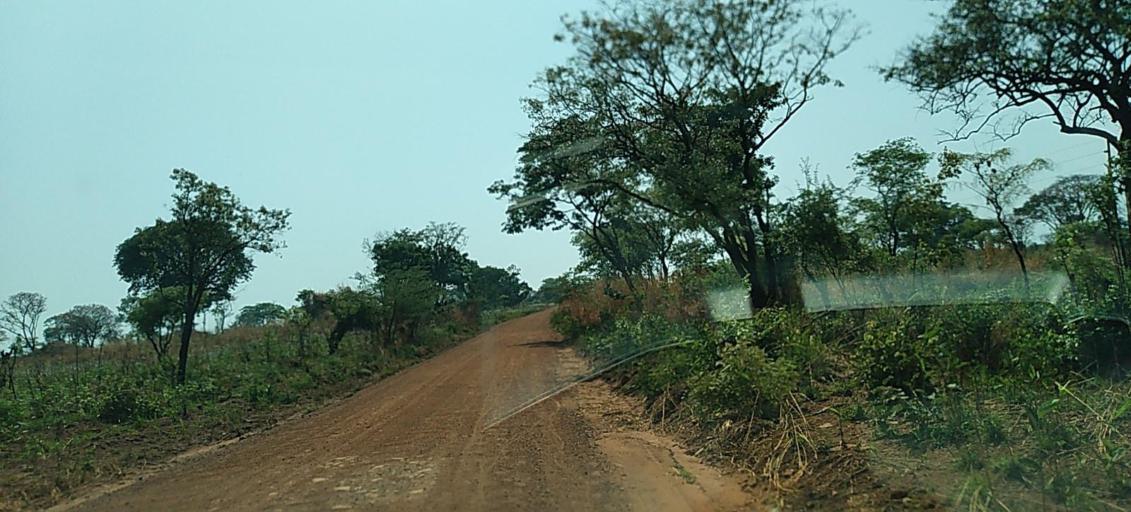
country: ZM
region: North-Western
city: Kansanshi
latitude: -12.0055
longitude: 26.5346
